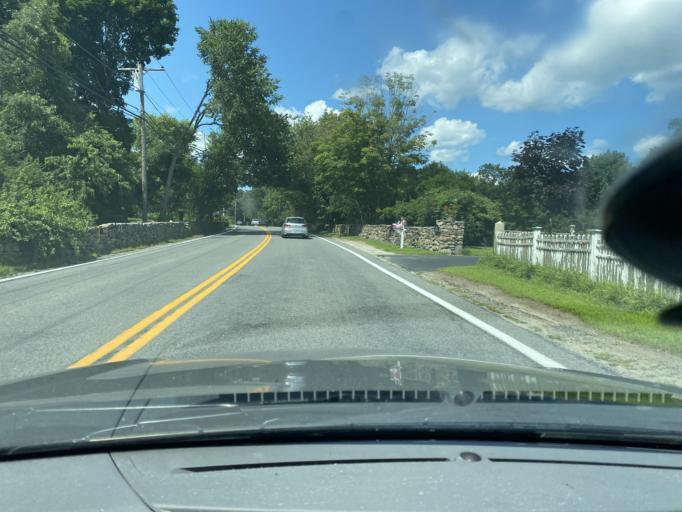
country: US
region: Rhode Island
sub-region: Providence County
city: North Scituate
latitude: 41.8448
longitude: -71.5850
